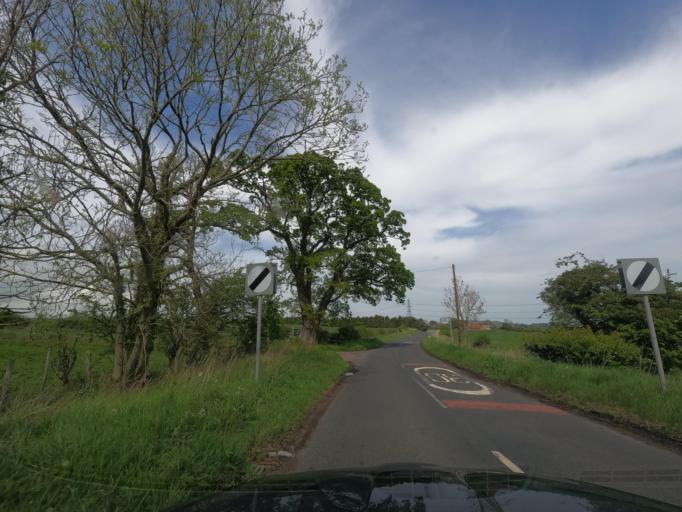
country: GB
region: England
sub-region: Northumberland
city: Whittingham
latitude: 55.4043
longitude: -1.8936
